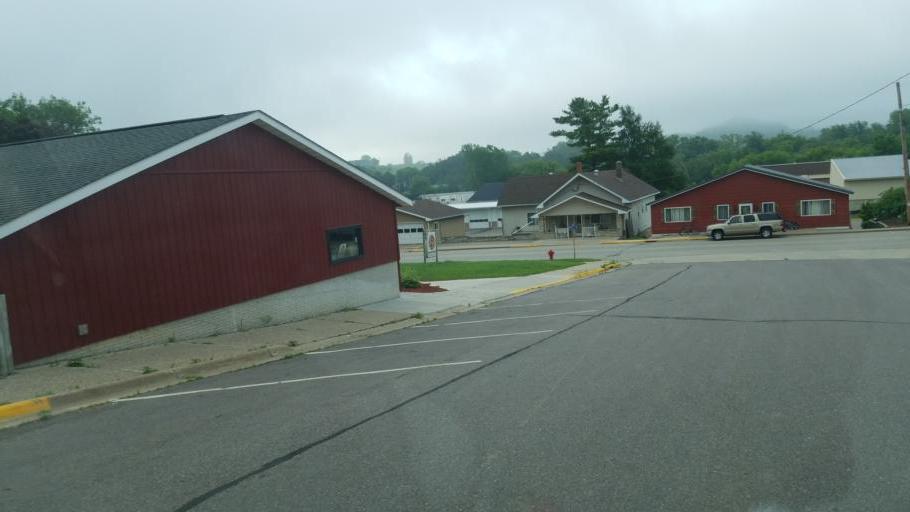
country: US
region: Wisconsin
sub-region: Vernon County
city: Hillsboro
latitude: 43.6529
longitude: -90.3383
